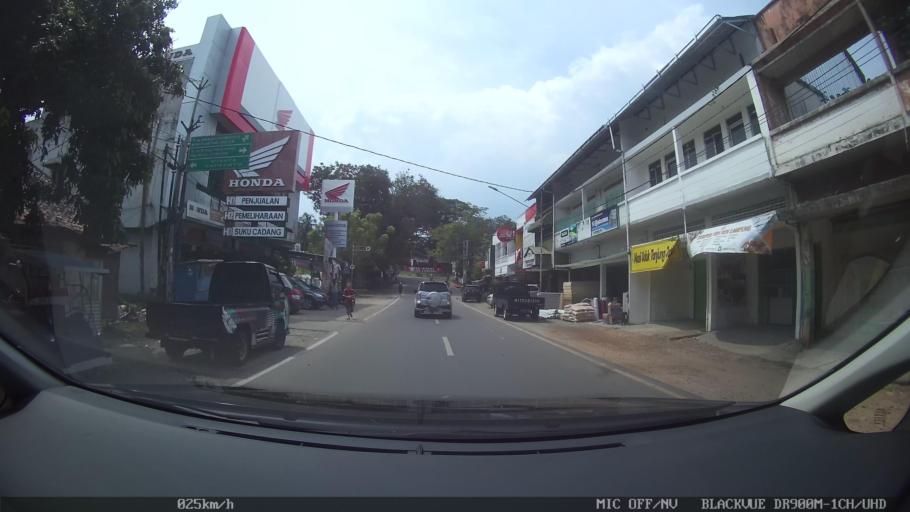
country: ID
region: Lampung
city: Bandarlampung
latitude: -5.4472
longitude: 105.2621
